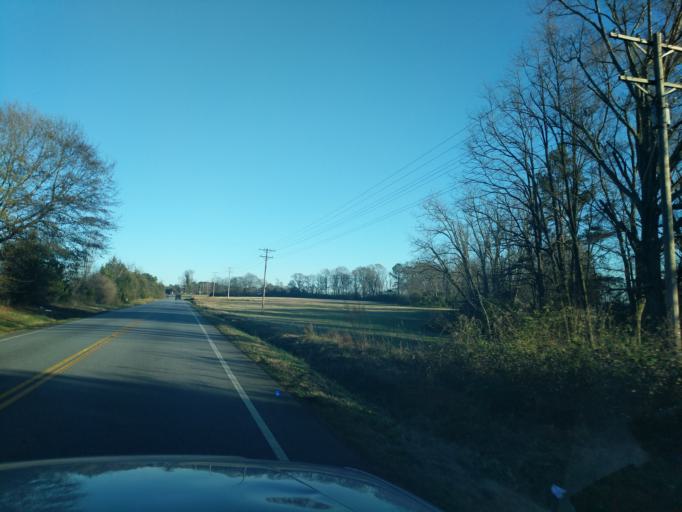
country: US
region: South Carolina
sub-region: Oconee County
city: Seneca
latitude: 34.5940
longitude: -82.9957
